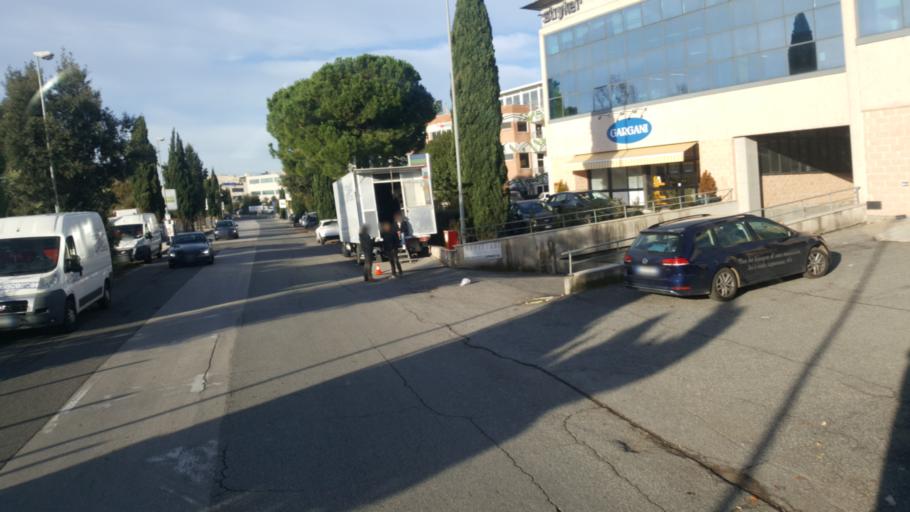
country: IT
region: Latium
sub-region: Citta metropolitana di Roma Capitale
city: Formello
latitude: 42.0494
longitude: 12.4032
